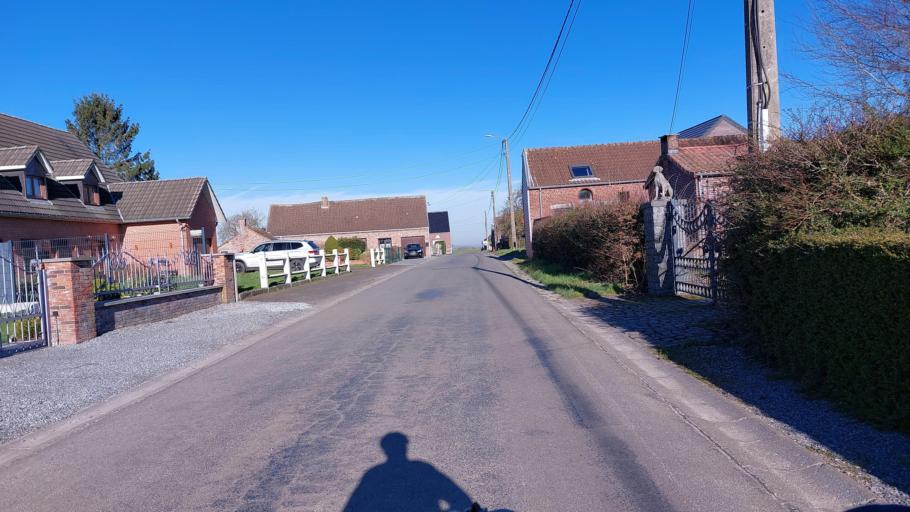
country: BE
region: Wallonia
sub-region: Province du Hainaut
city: Chievres
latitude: 50.5401
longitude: 3.8375
